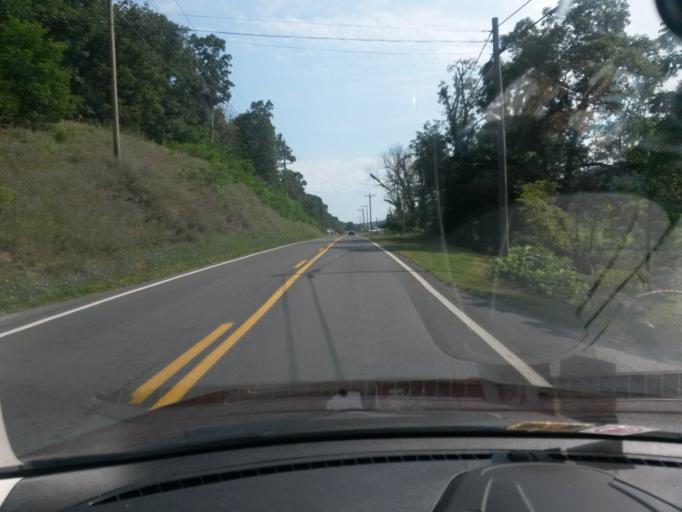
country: US
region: Virginia
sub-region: Shenandoah County
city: Basye
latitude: 39.0123
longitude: -78.7677
